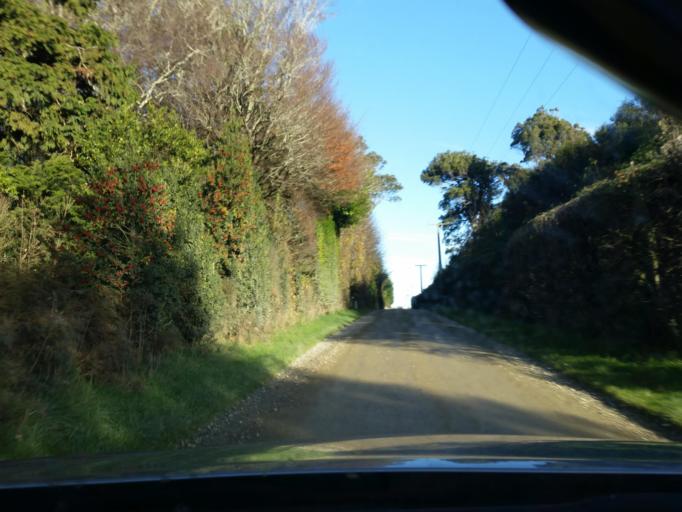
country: NZ
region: Southland
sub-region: Invercargill City
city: Invercargill
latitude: -46.3215
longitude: 168.4788
